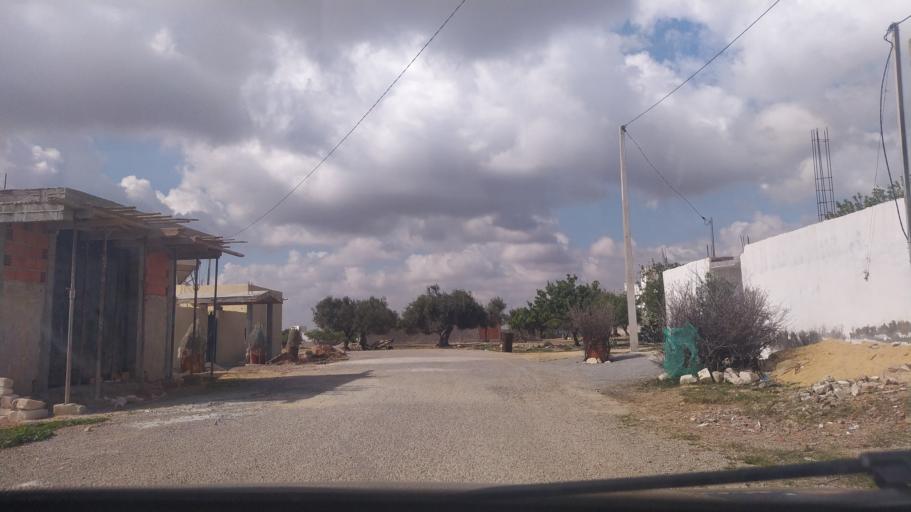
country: TN
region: Al Munastir
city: Sidi Bin Nur
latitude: 35.5273
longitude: 10.9425
